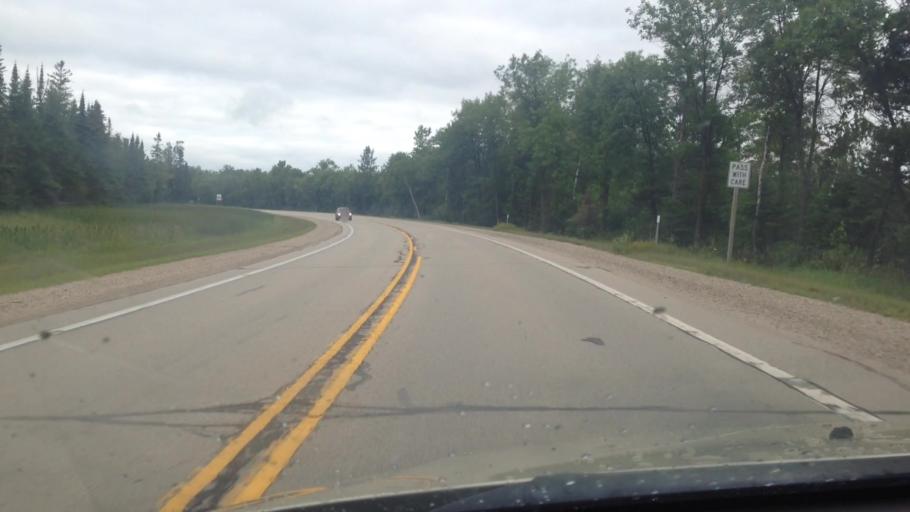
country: US
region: Michigan
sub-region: Menominee County
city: Menominee
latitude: 45.4193
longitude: -87.3465
